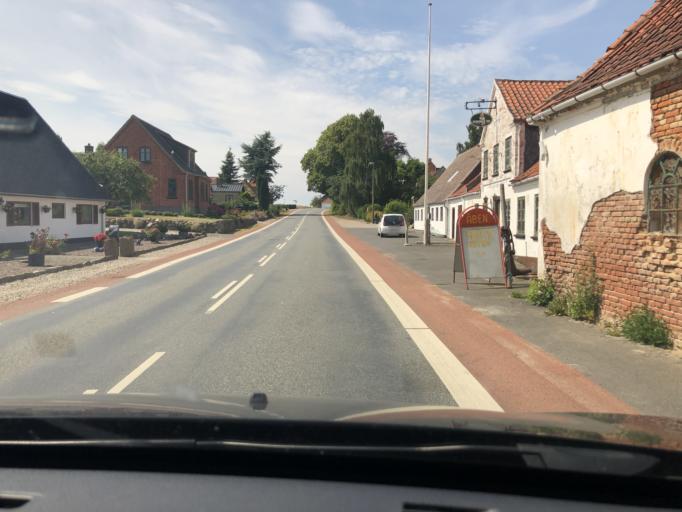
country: DK
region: South Denmark
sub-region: AEro Kommune
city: AEroskobing
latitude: 54.8885
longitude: 10.3181
